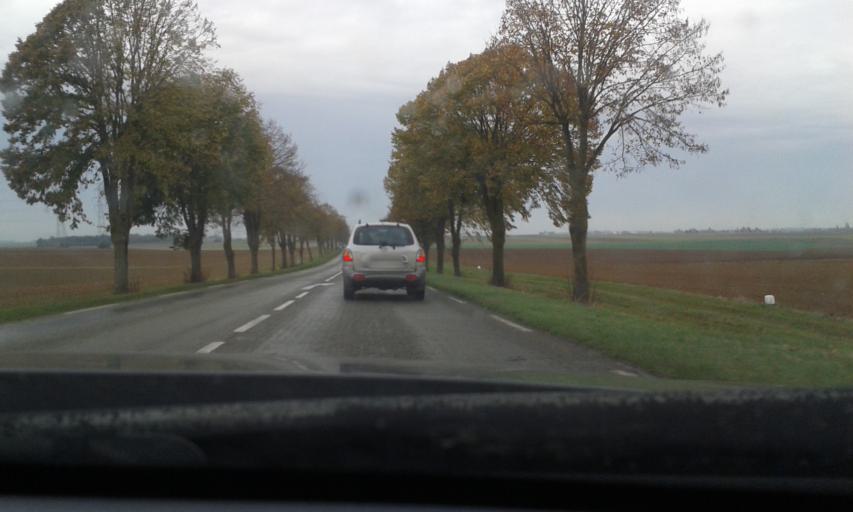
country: FR
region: Centre
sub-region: Departement d'Eure-et-Loir
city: Baigneaux
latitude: 48.1541
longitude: 1.8434
